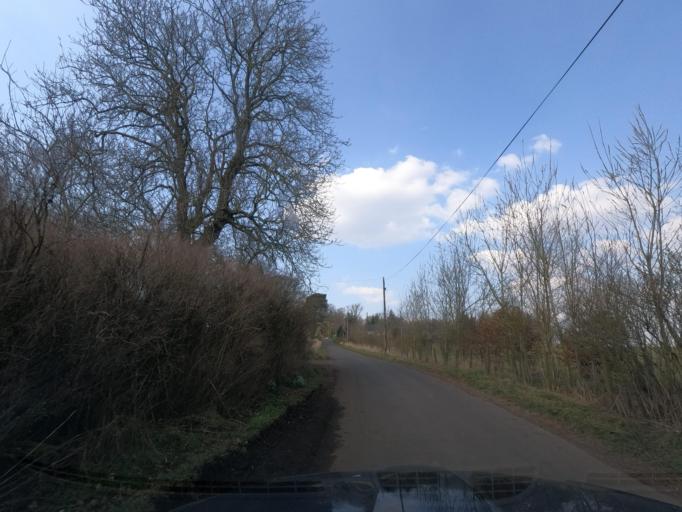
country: GB
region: Scotland
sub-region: South Lanarkshire
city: Carnwath
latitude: 55.7428
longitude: -3.6289
